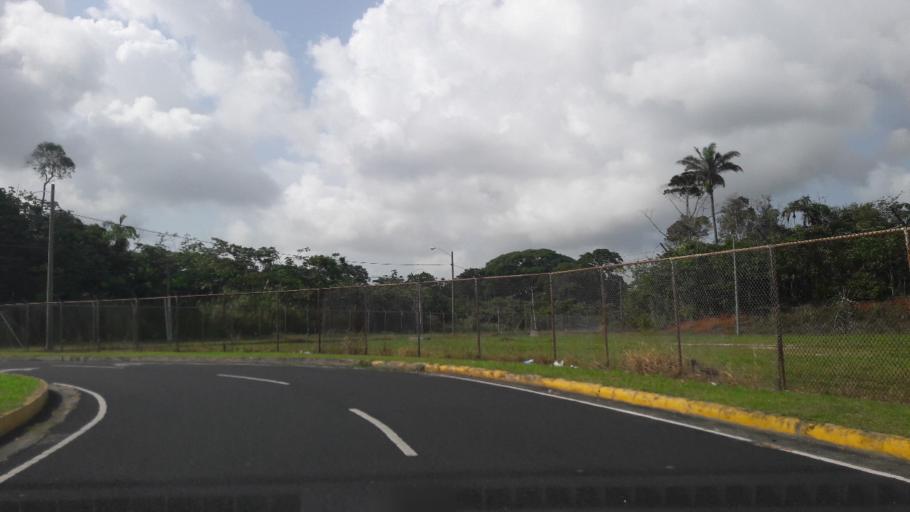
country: PA
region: Colon
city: Cativa
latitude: 9.3586
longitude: -79.8636
